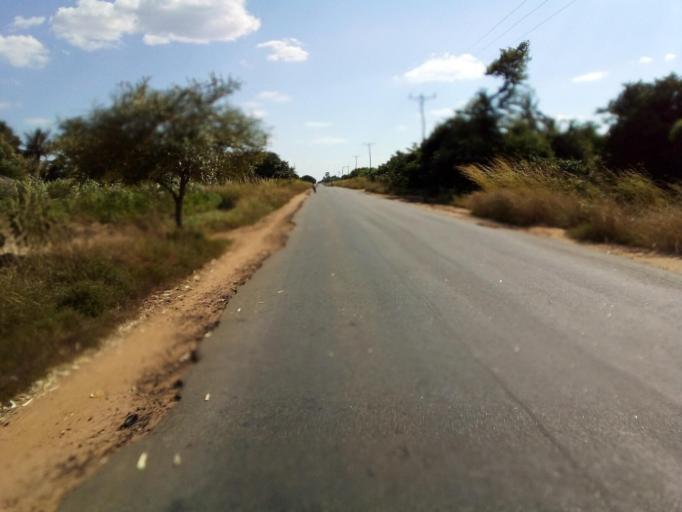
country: MZ
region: Zambezia
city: Quelimane
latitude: -17.5775
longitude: 36.6716
